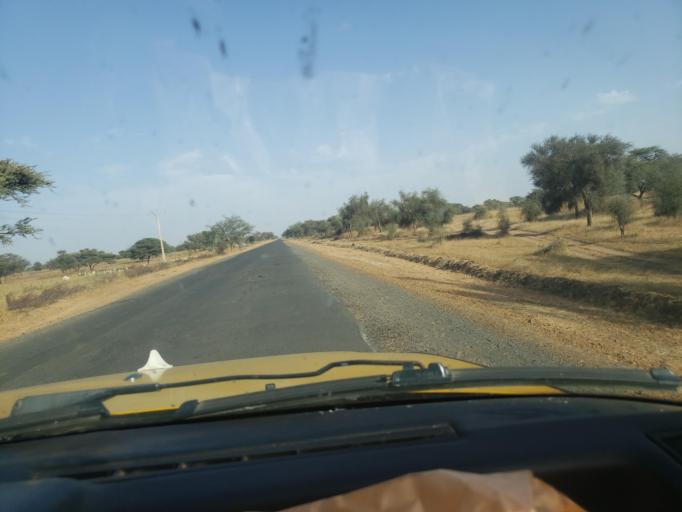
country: SN
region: Louga
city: Louga
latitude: 15.5064
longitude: -15.9642
